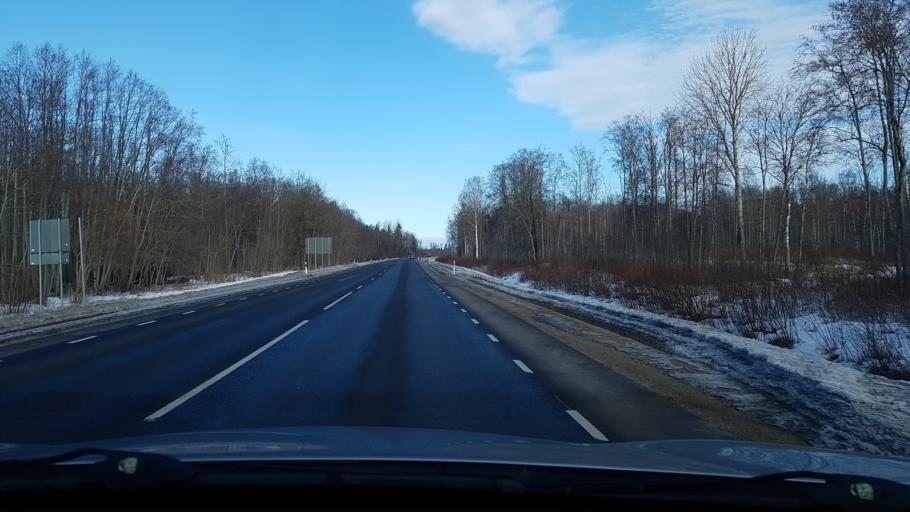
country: EE
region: Viljandimaa
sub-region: Viljandi linn
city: Viljandi
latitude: 58.3793
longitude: 25.5616
